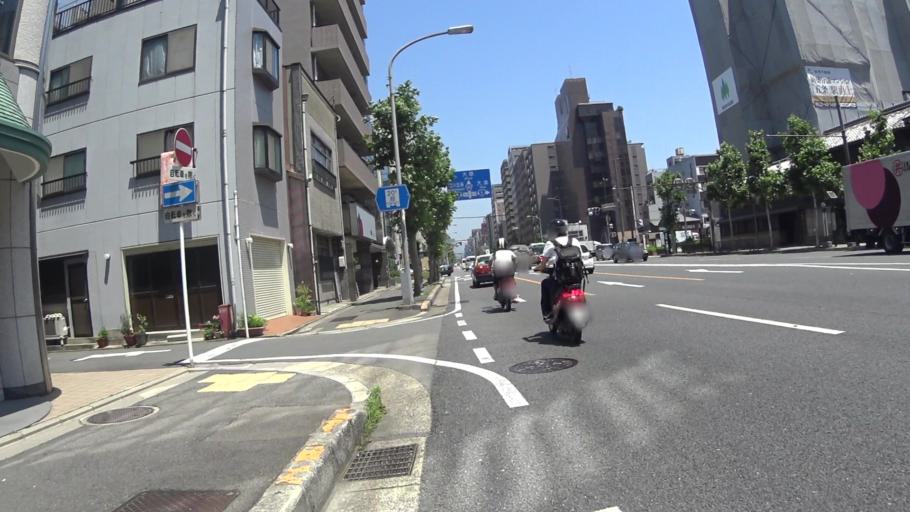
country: JP
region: Kyoto
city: Kyoto
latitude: 34.9953
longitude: 135.7596
